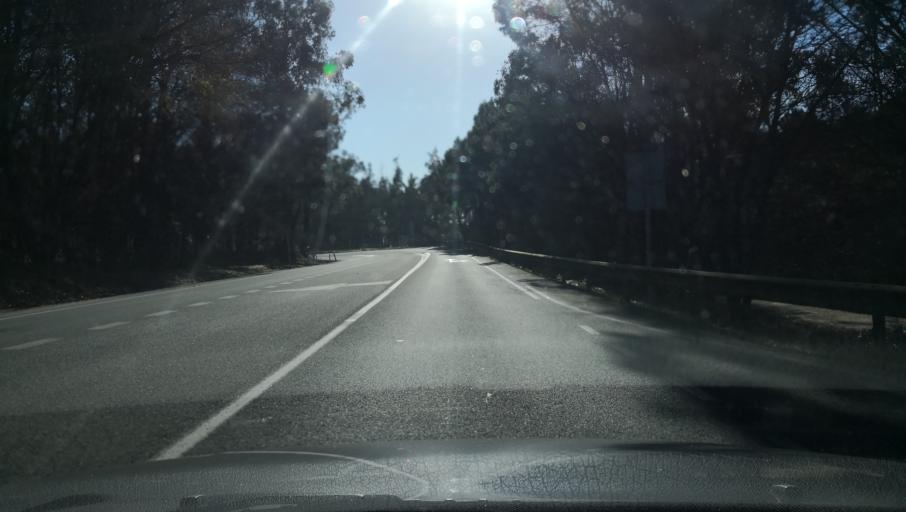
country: ES
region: Galicia
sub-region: Provincia da Coruna
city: Vedra
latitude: 42.7915
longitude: -8.4589
